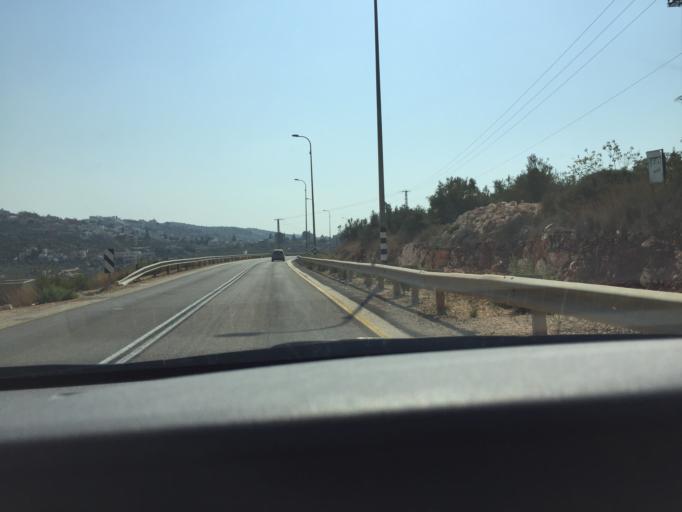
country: PS
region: West Bank
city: Kafr ad Dik
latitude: 32.0766
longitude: 35.0875
